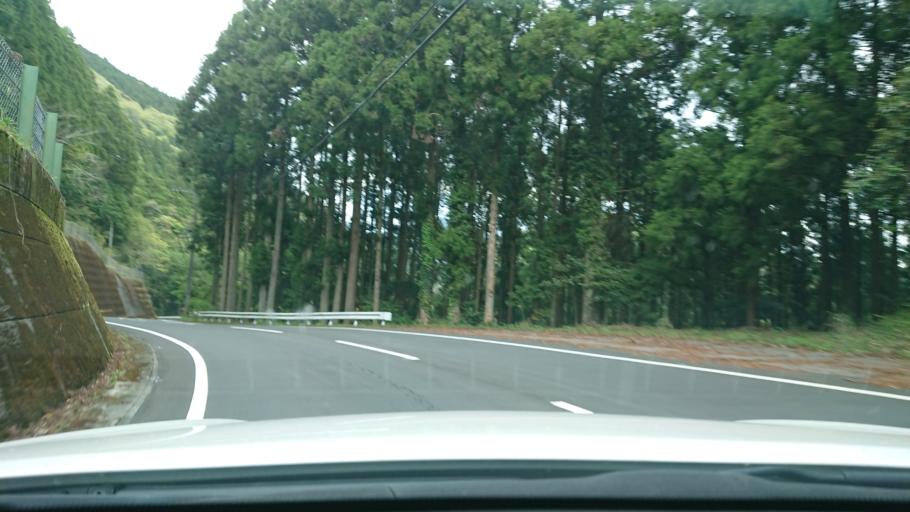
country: JP
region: Tokushima
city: Ishii
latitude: 33.9059
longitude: 134.4209
